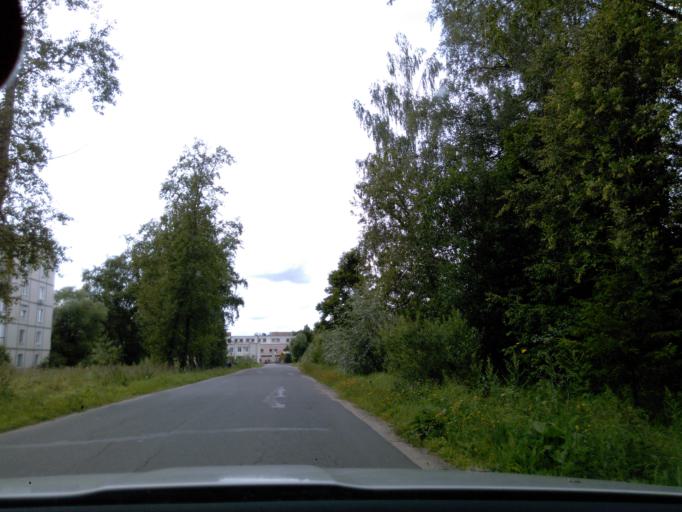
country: RU
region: Tverskaya
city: Konakovo
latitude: 56.6834
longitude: 36.7019
